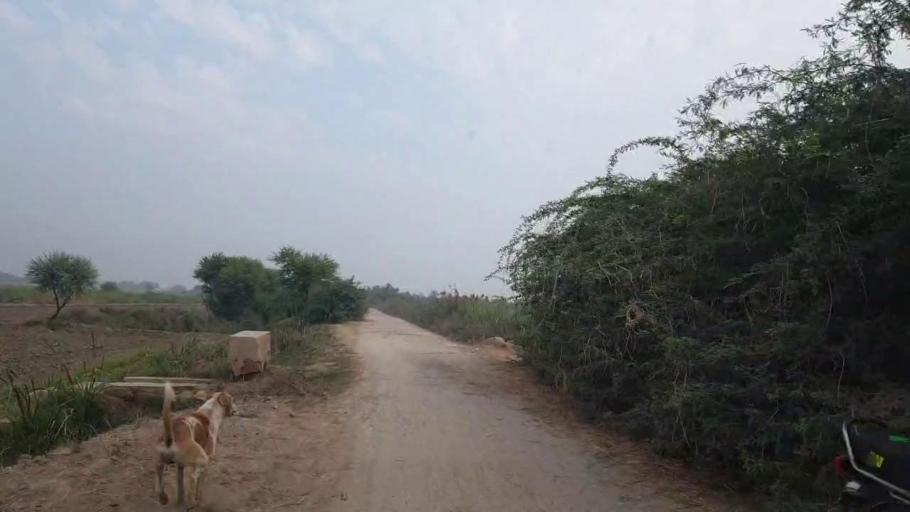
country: PK
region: Sindh
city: Talhar
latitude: 24.8306
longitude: 68.8803
